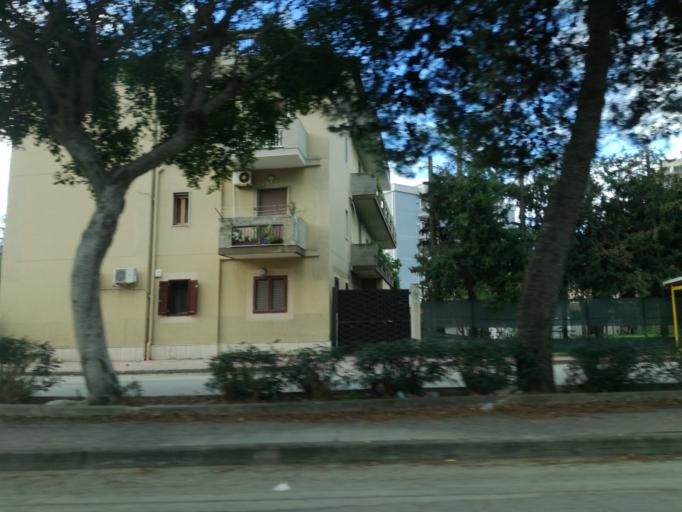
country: IT
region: Sicily
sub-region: Provincia di Caltanissetta
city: Gela
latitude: 37.0785
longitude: 14.2182
